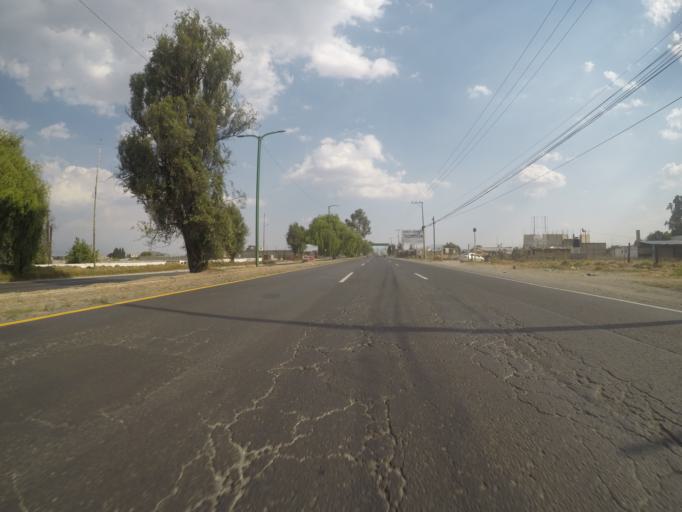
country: MX
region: Morelos
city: San Miguel Totocuitlapilco
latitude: 19.2248
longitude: -99.5940
